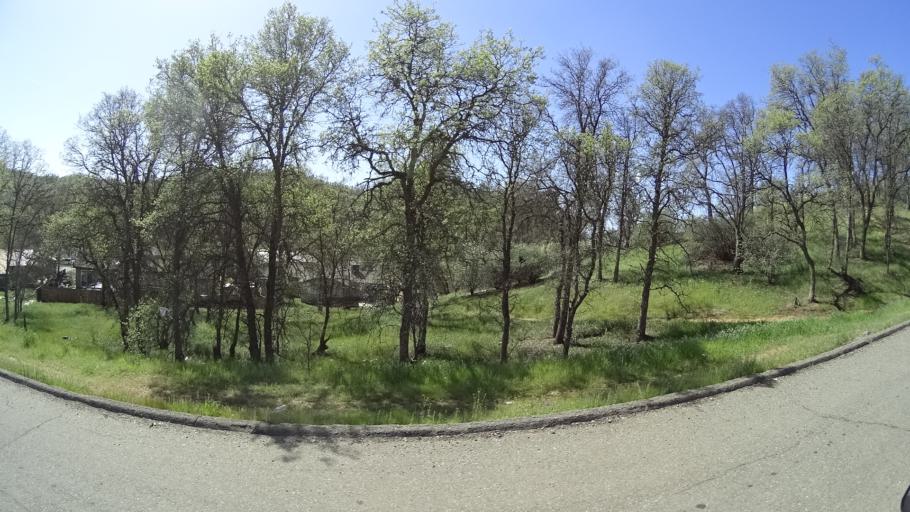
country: US
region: California
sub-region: Glenn County
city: Orland
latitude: 39.6740
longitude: -122.5198
